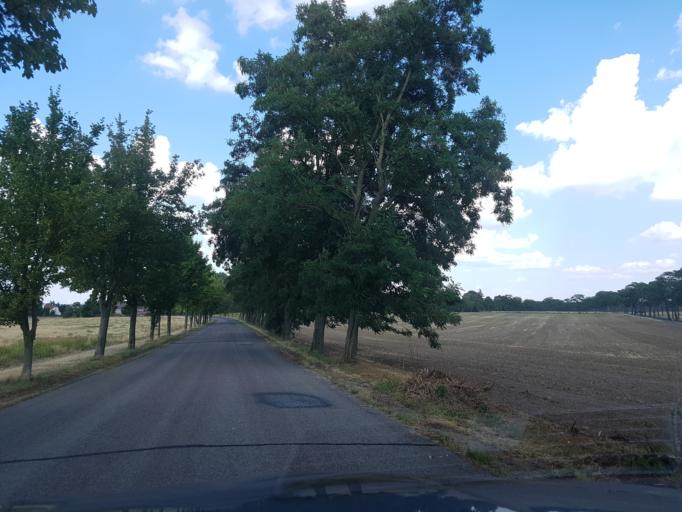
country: DE
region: Brandenburg
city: Schlieben
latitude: 51.6808
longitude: 13.3460
